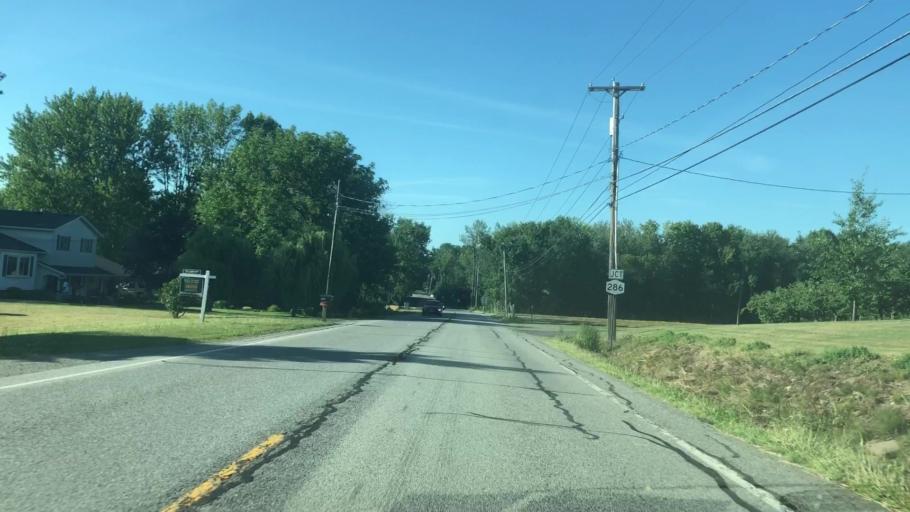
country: US
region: New York
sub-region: Wayne County
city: Ontario
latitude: 43.1626
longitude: -77.2901
